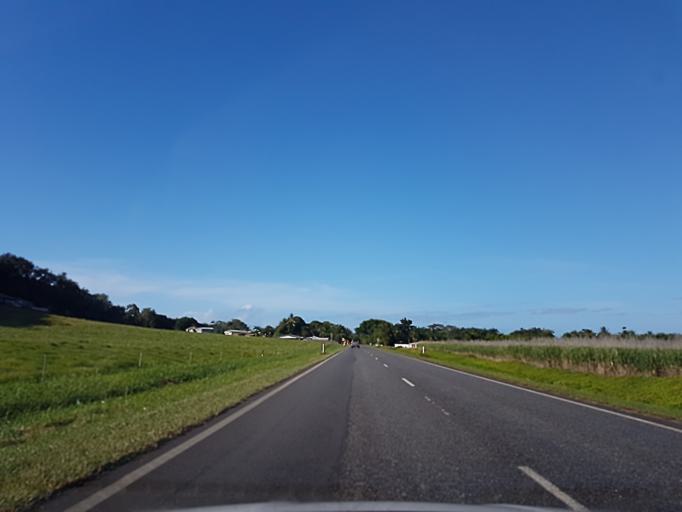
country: AU
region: Queensland
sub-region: Cairns
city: Port Douglas
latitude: -16.3914
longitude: 145.4135
